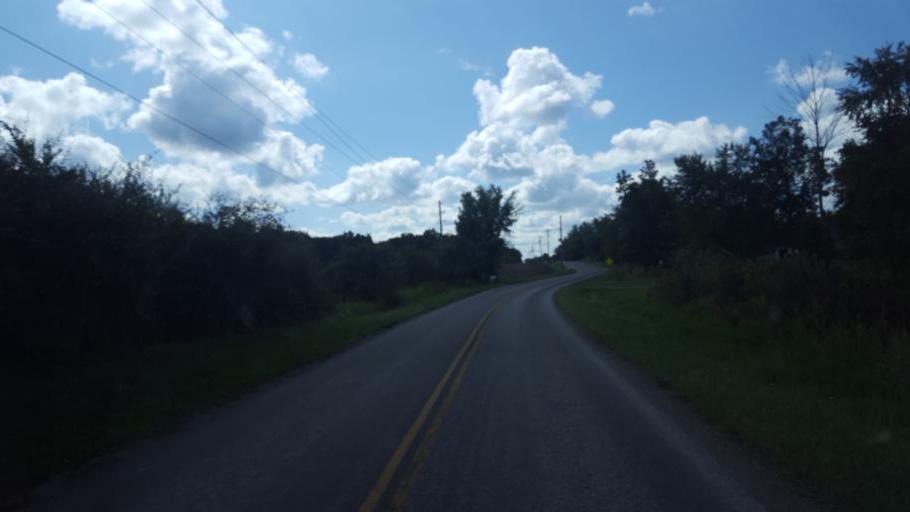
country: US
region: Ohio
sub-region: Wayne County
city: West Salem
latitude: 41.0121
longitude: -82.1266
